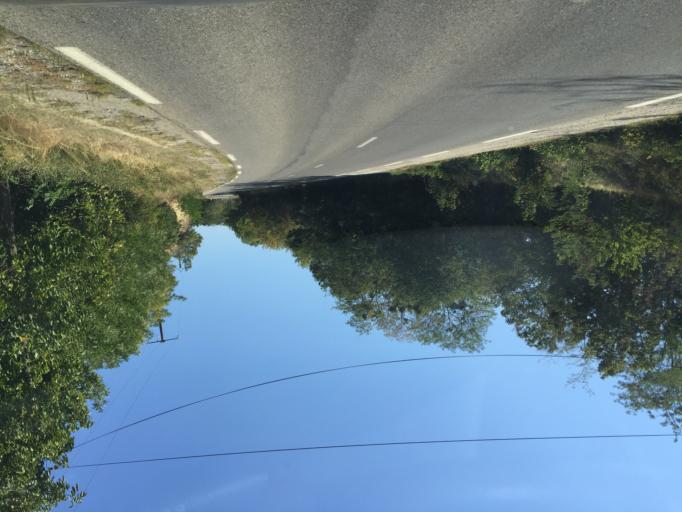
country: FR
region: Provence-Alpes-Cote d'Azur
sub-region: Departement des Alpes-de-Haute-Provence
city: Forcalquier
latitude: 43.9569
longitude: 5.8049
